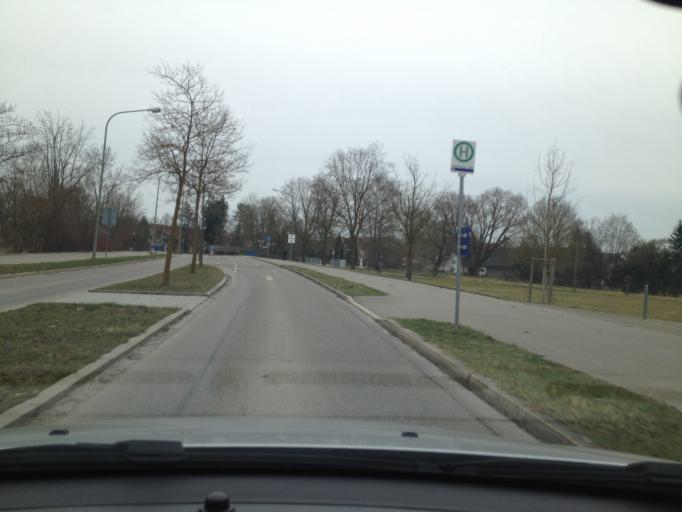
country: DE
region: Bavaria
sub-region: Swabia
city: Bobingen
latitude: 48.2688
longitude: 10.8246
